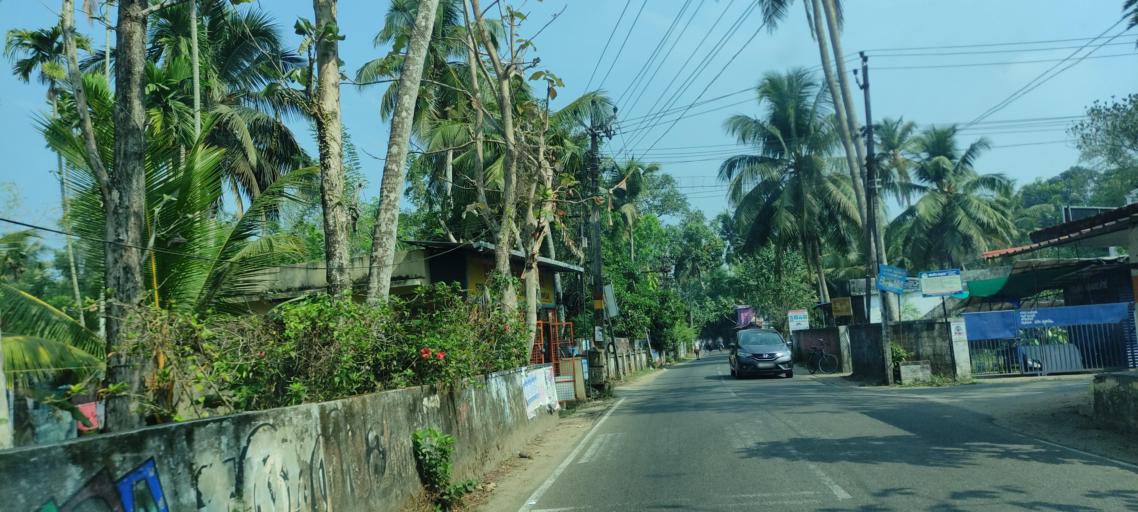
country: IN
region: Kerala
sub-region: Alappuzha
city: Kutiatodu
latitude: 9.7834
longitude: 76.3043
